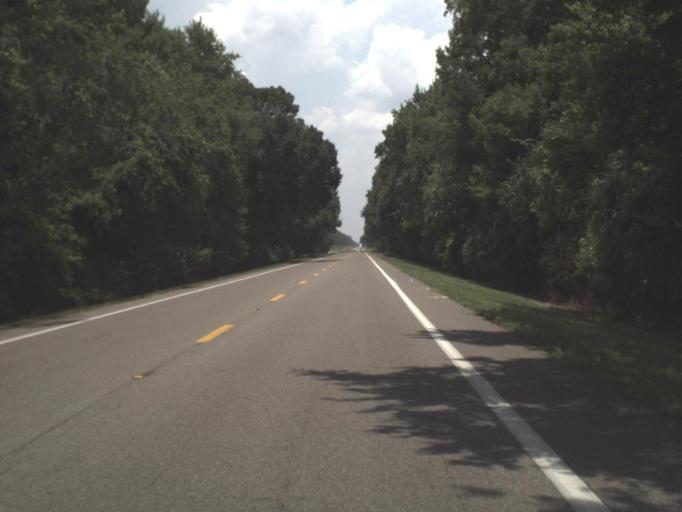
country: US
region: Florida
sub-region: Putnam County
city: Palatka
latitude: 29.4883
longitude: -81.7430
